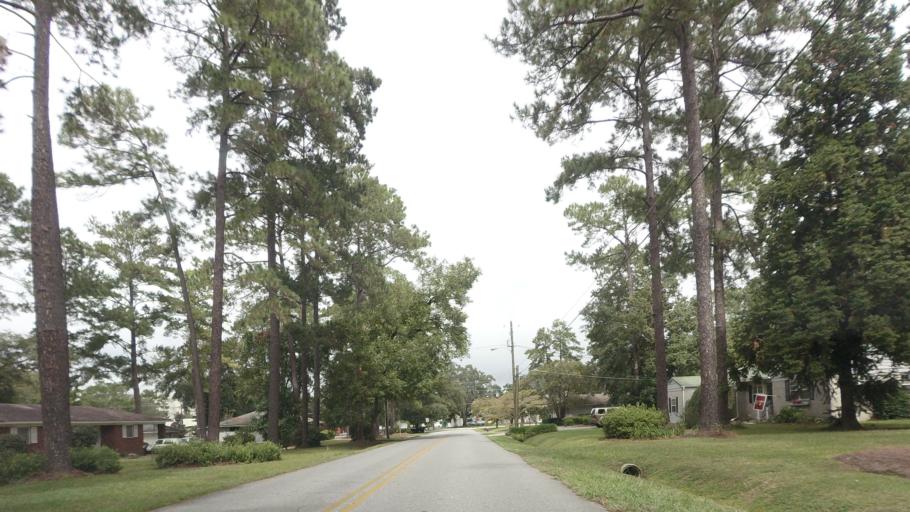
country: US
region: Georgia
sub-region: Lowndes County
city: Valdosta
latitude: 30.8587
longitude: -83.2845
